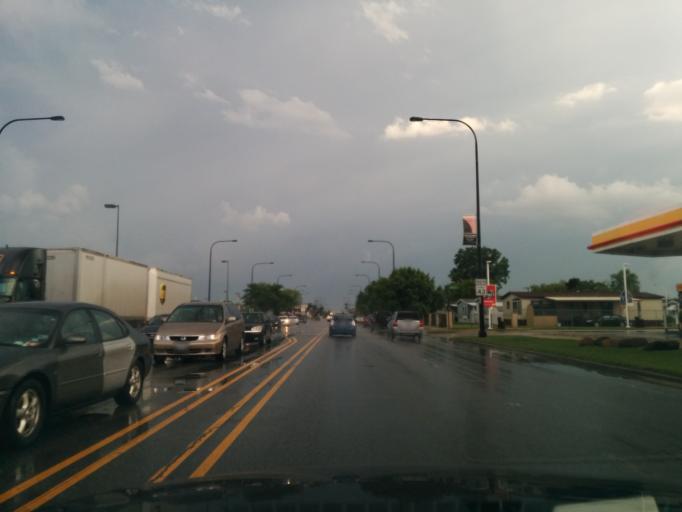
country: US
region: Illinois
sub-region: Cook County
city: Bridgeview
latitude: 41.7332
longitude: -87.7991
